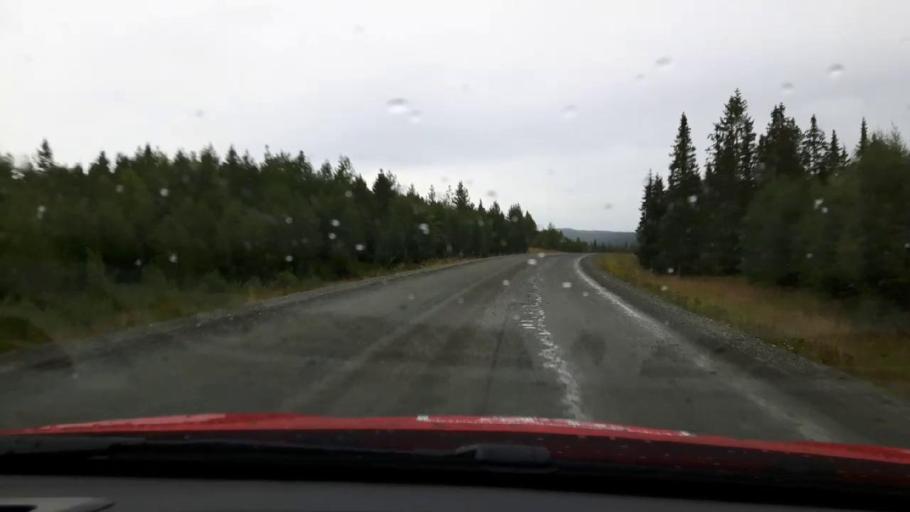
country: SE
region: Jaemtland
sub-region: Are Kommun
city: Are
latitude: 63.4102
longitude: 12.7941
